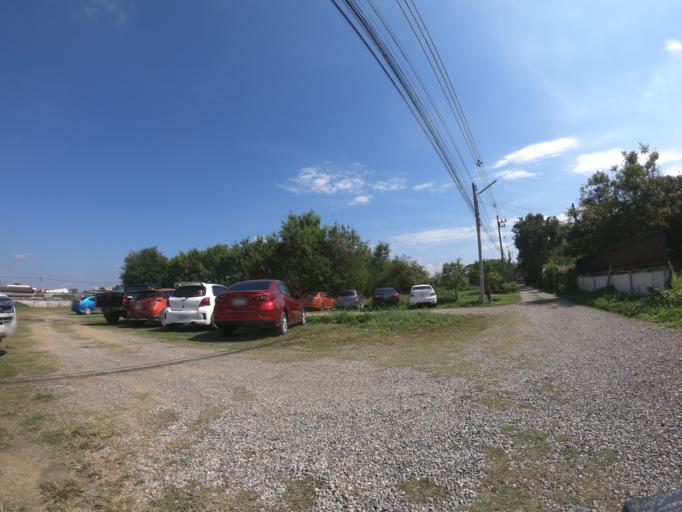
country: TH
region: Chiang Mai
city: Chiang Mai
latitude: 18.7413
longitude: 98.9560
